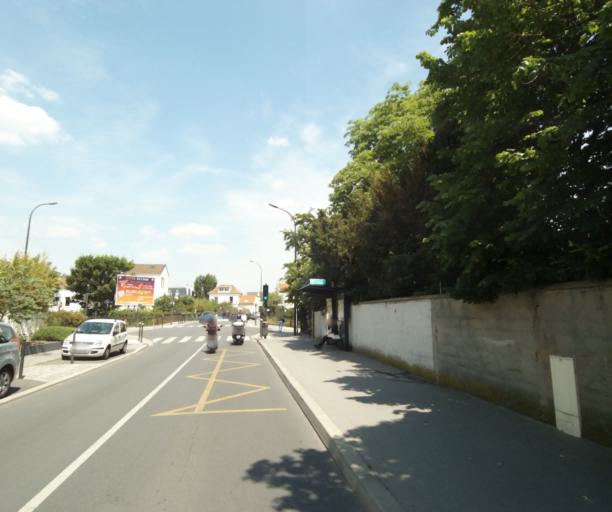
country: FR
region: Ile-de-France
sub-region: Departement des Hauts-de-Seine
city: Bois-Colombes
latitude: 48.9131
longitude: 2.2654
